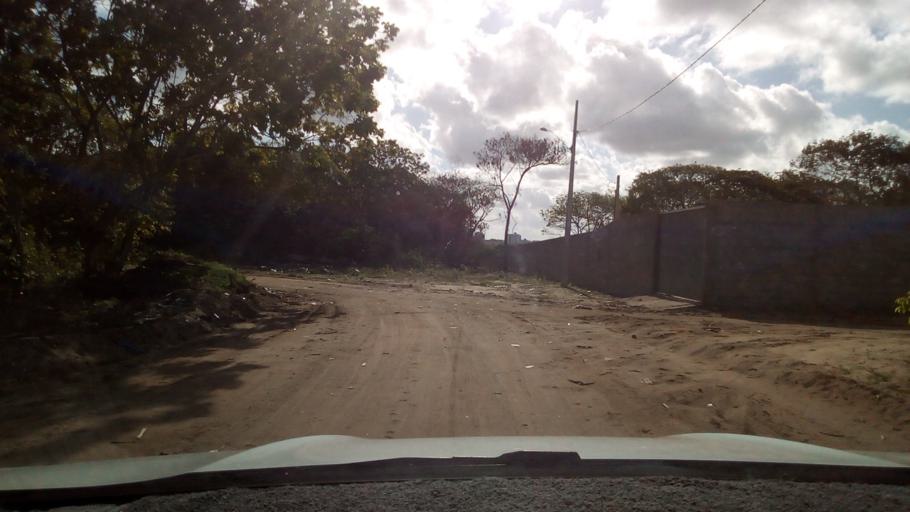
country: BR
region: Paraiba
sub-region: Joao Pessoa
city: Joao Pessoa
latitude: -7.1398
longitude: -34.8251
